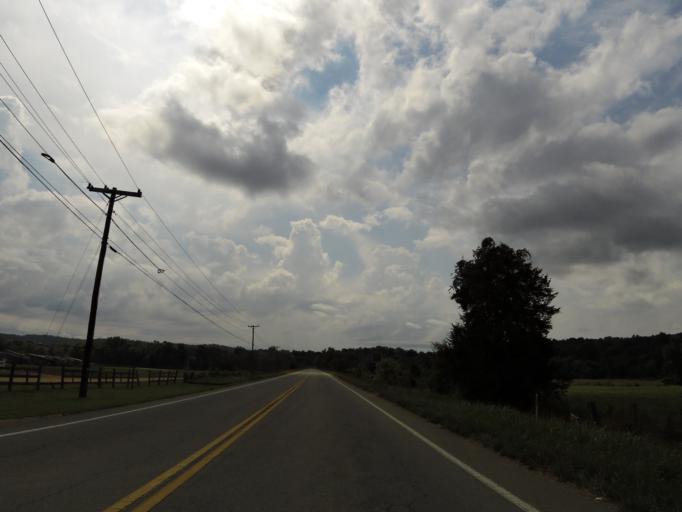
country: US
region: Tennessee
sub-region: Perry County
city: Linden
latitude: 35.8165
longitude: -87.7815
